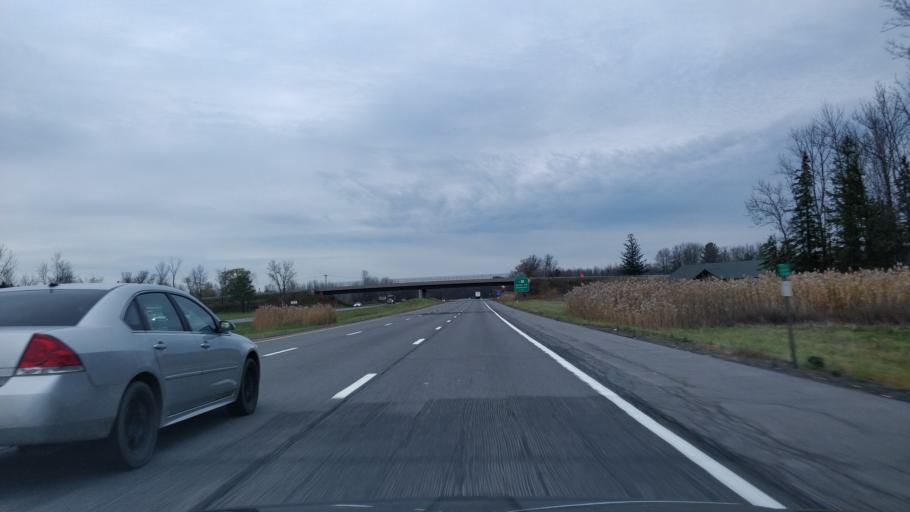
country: US
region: New York
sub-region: Onondaga County
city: Brewerton
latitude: 43.2144
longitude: -76.1293
